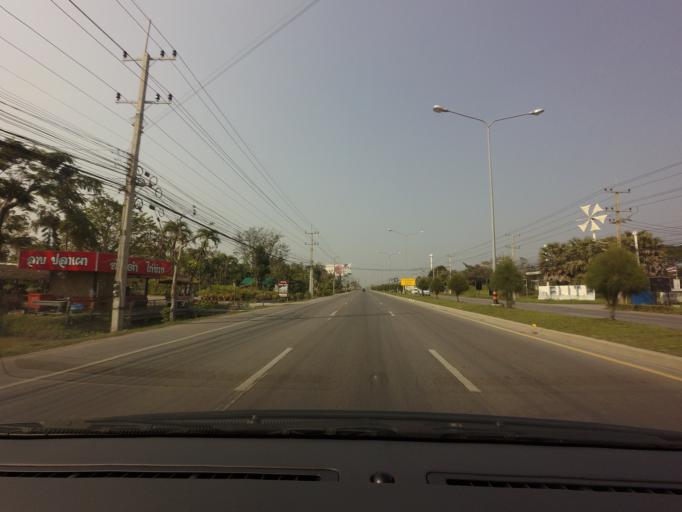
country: TH
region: Prachuap Khiri Khan
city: Hua Hin
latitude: 12.6638
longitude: 99.9520
